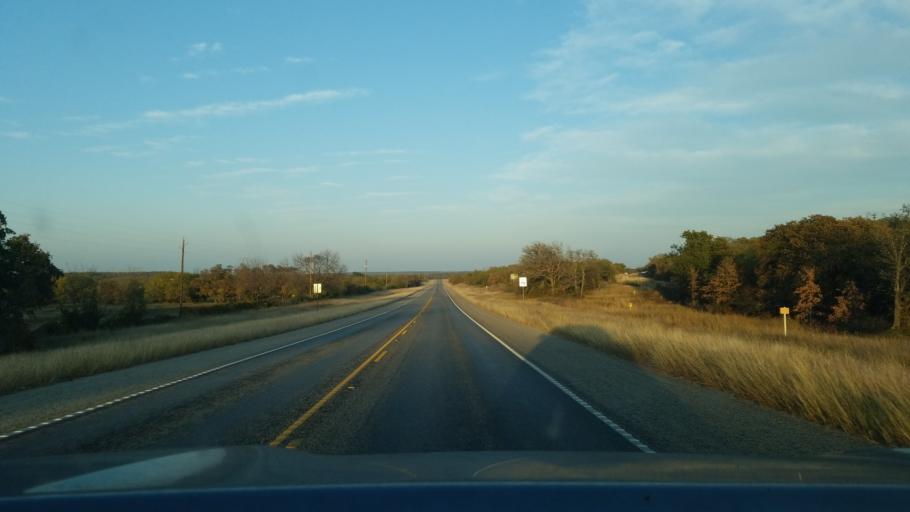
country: US
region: Texas
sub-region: Eastland County
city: Cisco
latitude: 32.4017
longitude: -98.9613
